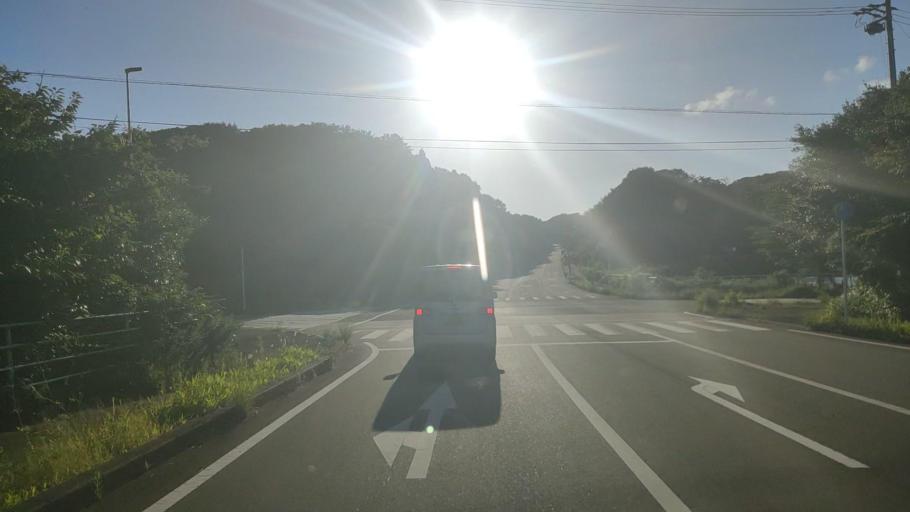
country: JP
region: Mie
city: Toba
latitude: 34.2694
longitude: 136.7936
